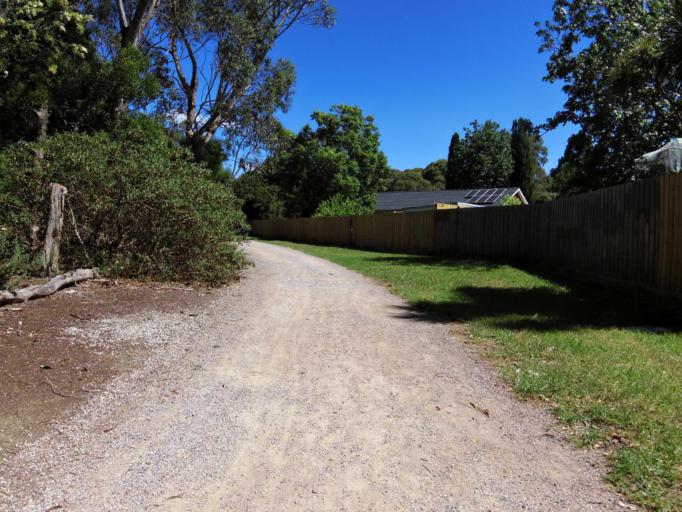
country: AU
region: Victoria
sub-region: Maroondah
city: Croydon North
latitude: -37.7798
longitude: 145.3058
